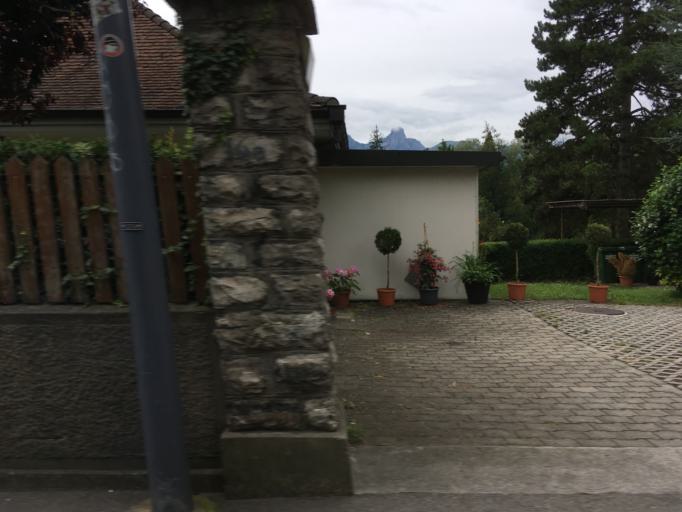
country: CH
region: Bern
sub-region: Thun District
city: Thun
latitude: 46.7549
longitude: 7.6354
